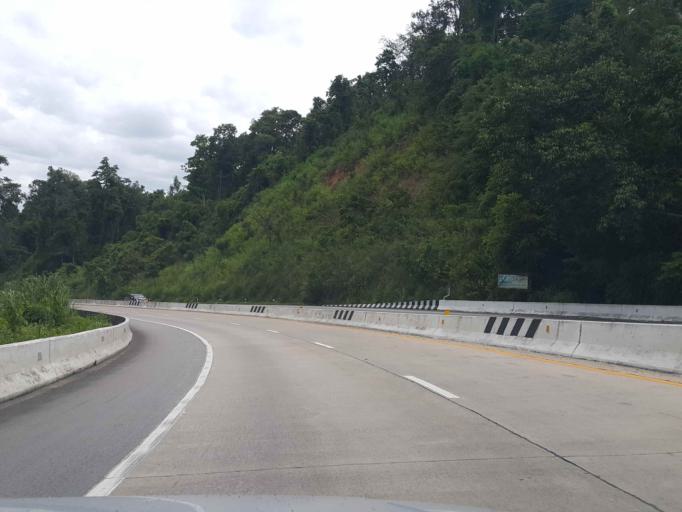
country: TH
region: Lamphun
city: Mae Tha
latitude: 18.4112
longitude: 99.2097
